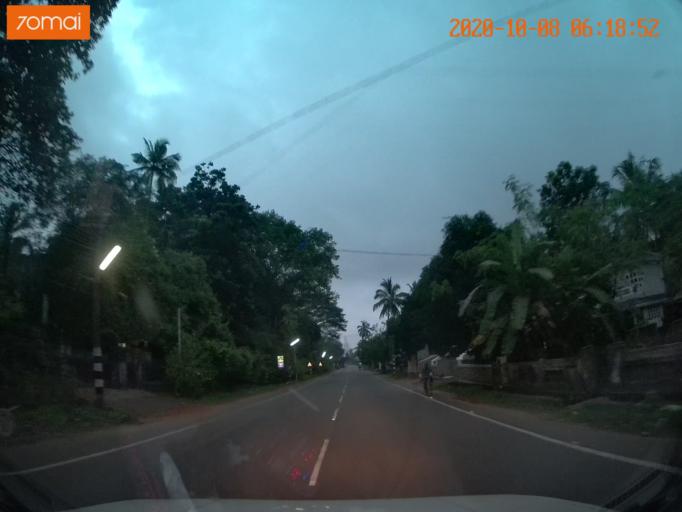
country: IN
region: Kerala
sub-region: Thrissur District
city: Trichur
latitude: 10.5141
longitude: 76.2432
